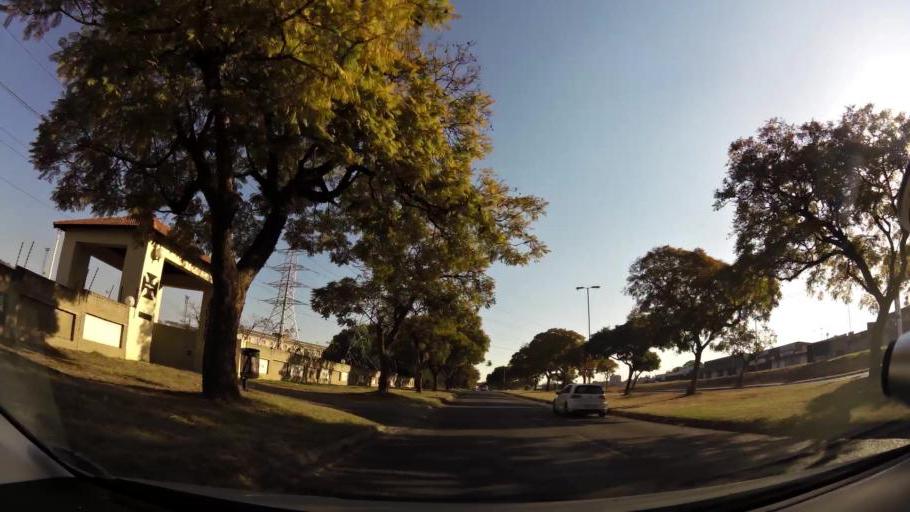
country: ZA
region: Gauteng
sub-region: City of Tshwane Metropolitan Municipality
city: Pretoria
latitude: -25.7596
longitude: 28.1387
